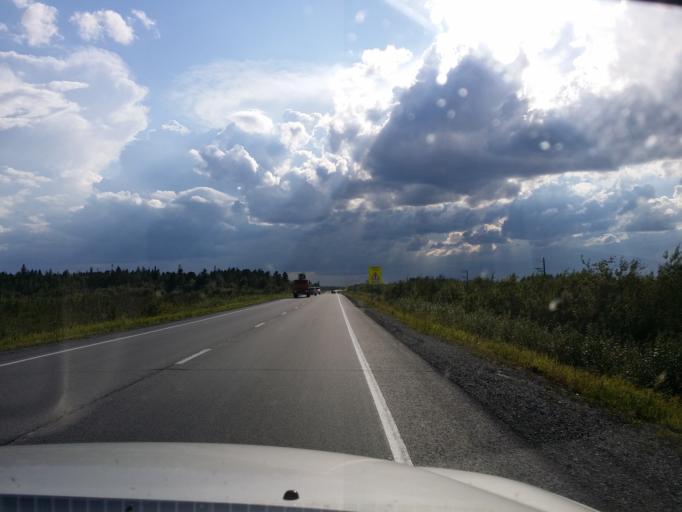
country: RU
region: Khanty-Mansiyskiy Avtonomnyy Okrug
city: Surgut
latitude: 61.4543
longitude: 74.0583
